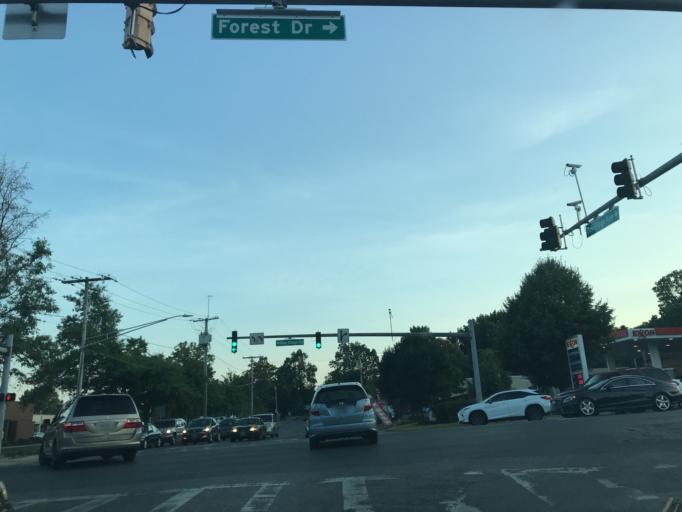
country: US
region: Maryland
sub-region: Anne Arundel County
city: Hillsmere Shores
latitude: 38.9502
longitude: -76.4925
